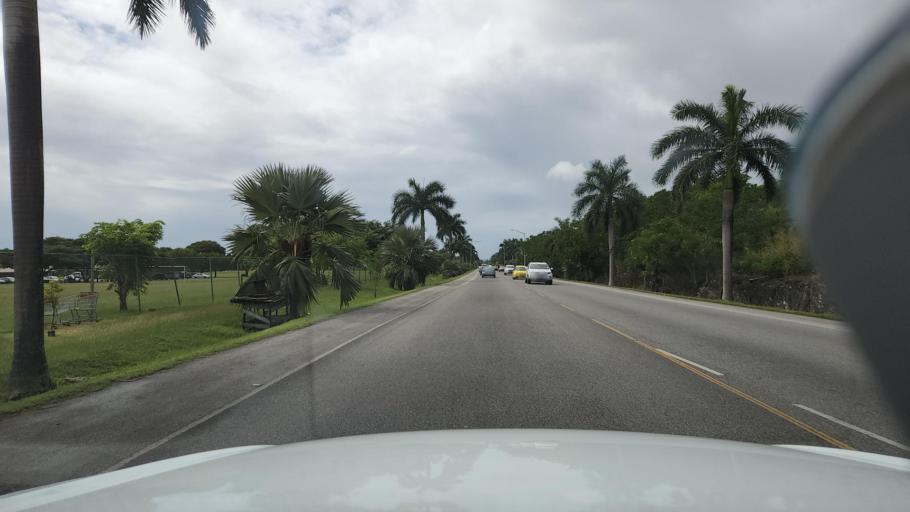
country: BB
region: Christ Church
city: Oistins
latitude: 13.0801
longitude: -59.5509
